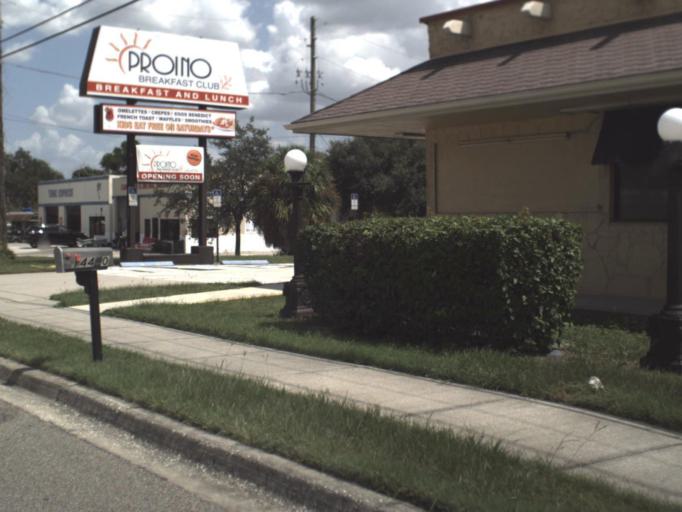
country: US
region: Florida
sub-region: Pinellas County
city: Indian Rocks Beach
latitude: 27.8803
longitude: -82.8378
